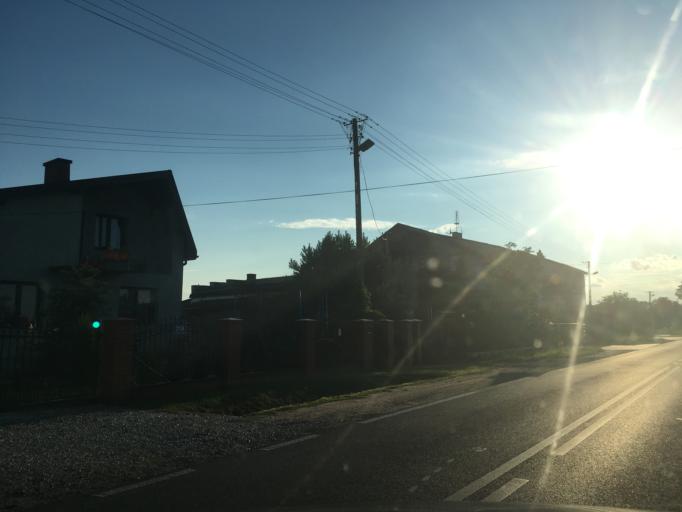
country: PL
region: Masovian Voivodeship
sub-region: Powiat grodziski
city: Grodzisk Mazowiecki
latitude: 52.1176
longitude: 20.5808
